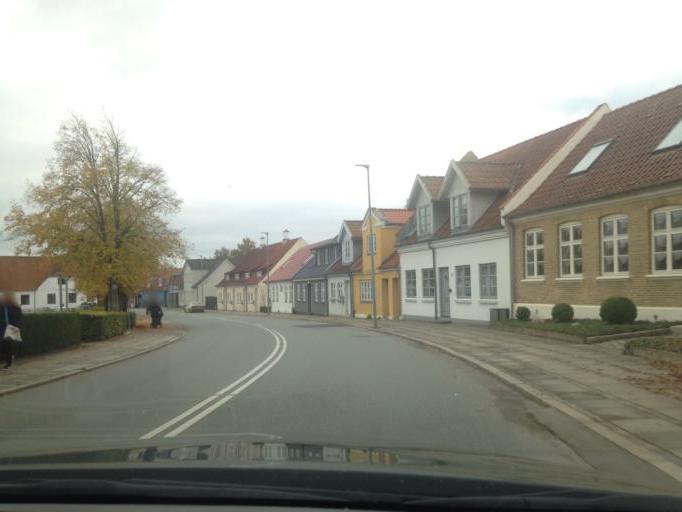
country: DK
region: South Denmark
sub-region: Kolding Kommune
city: Kolding
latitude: 55.4951
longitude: 9.4705
